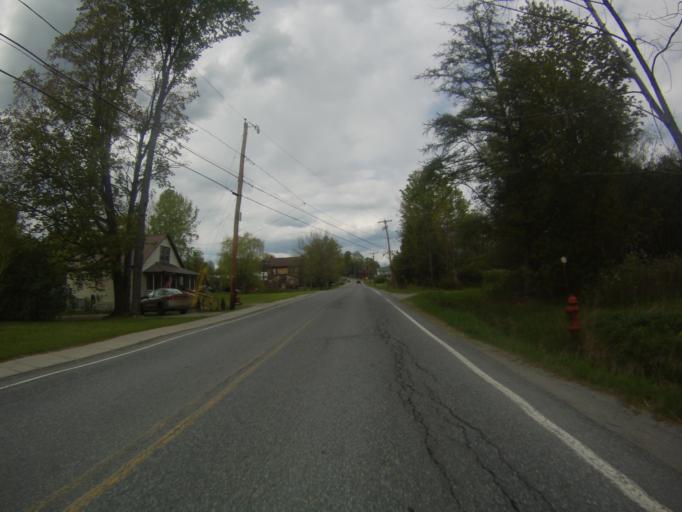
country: US
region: New York
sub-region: Essex County
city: Port Henry
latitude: 44.0432
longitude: -73.5046
